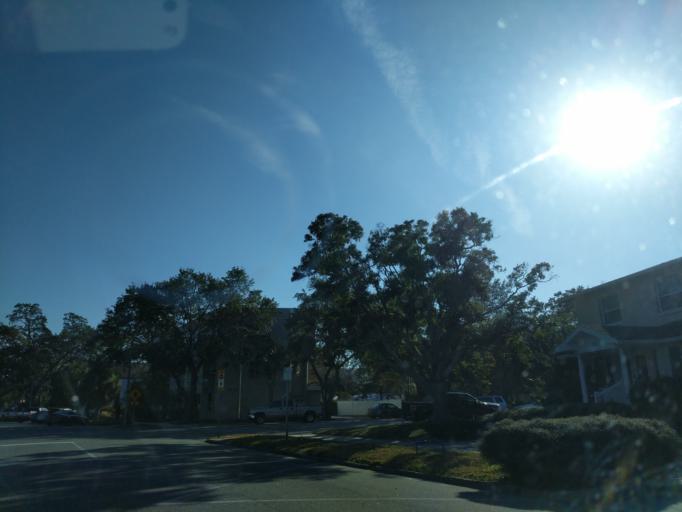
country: US
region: Florida
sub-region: Pinellas County
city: Saint Petersburg
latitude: 27.7739
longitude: -82.6436
